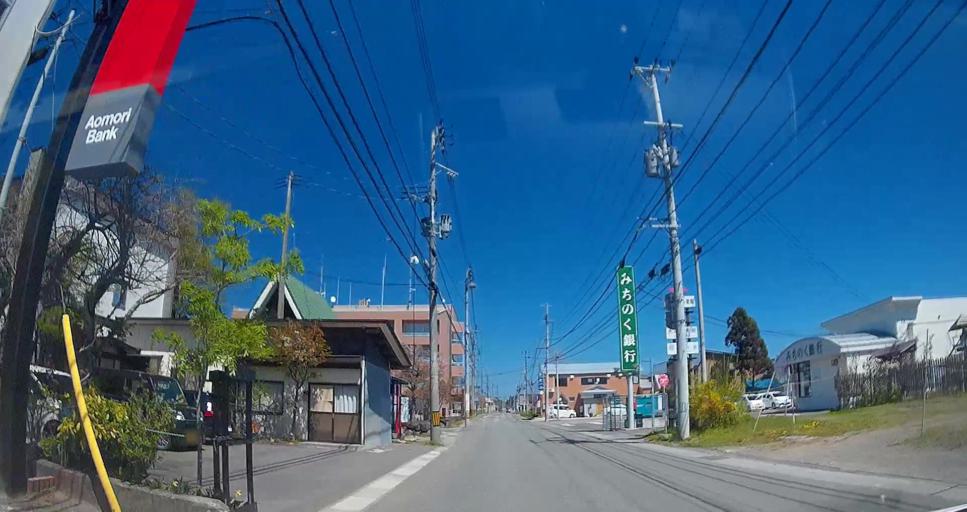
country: JP
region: Aomori
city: Misawa
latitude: 40.9665
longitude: 141.3749
